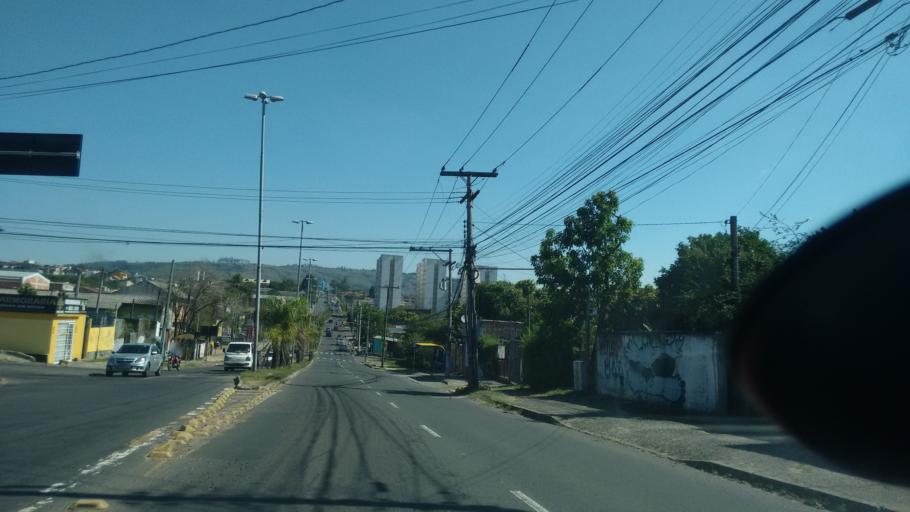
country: BR
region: Rio Grande do Sul
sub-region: Cachoeirinha
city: Cachoeirinha
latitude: -30.0157
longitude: -51.1193
